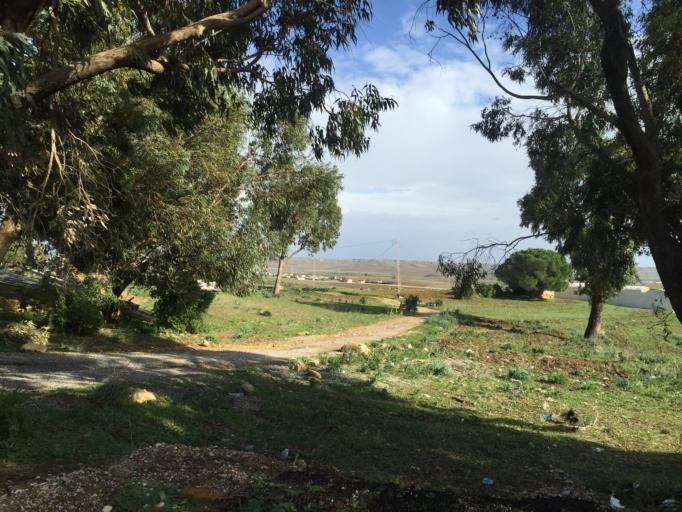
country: TN
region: Nabul
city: El Mida
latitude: 36.7909
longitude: 10.8514
